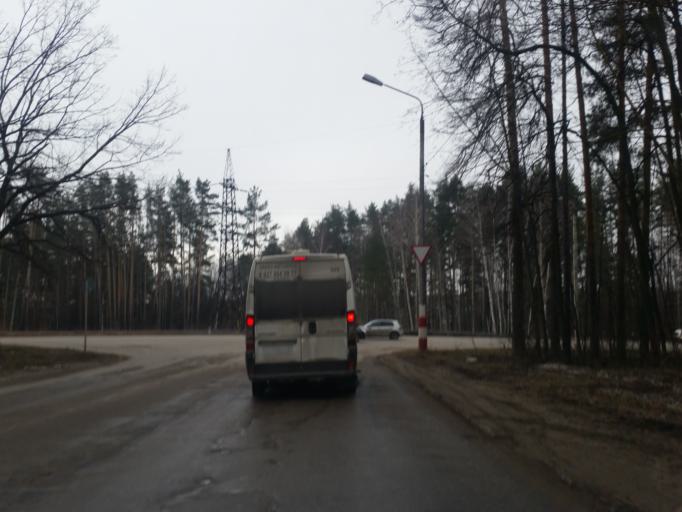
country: RU
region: Ulyanovsk
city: Dimitrovgrad
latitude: 54.2162
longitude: 49.5473
